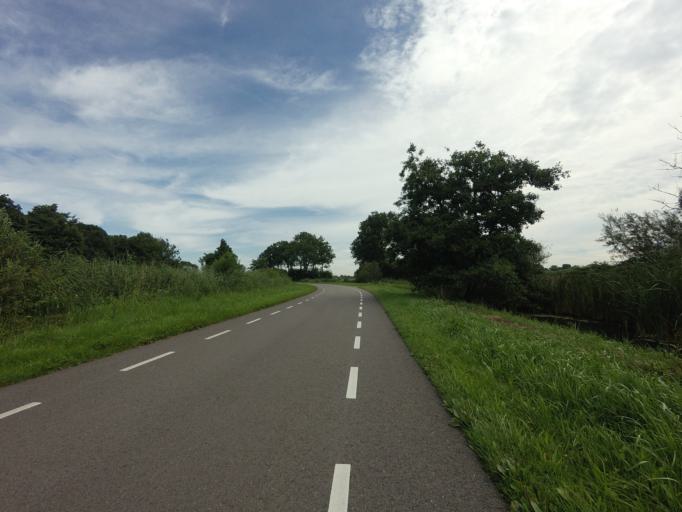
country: NL
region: Utrecht
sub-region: Stichtse Vecht
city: Breukelen
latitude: 52.1861
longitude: 4.9570
